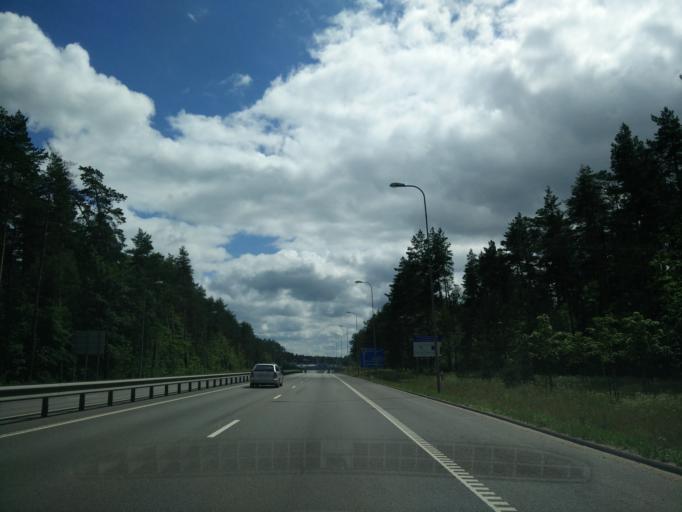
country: LT
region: Vilnius County
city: Lazdynai
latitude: 54.6399
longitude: 25.1512
